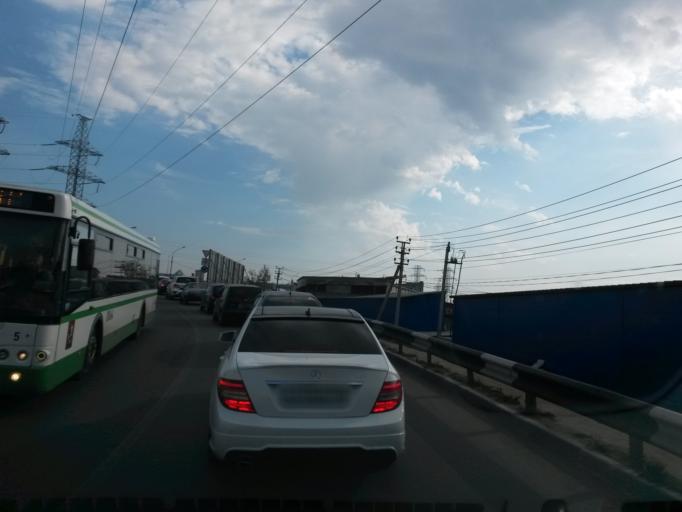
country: RU
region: Moscow
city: Tyoply Stan
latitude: 55.6047
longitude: 37.4827
